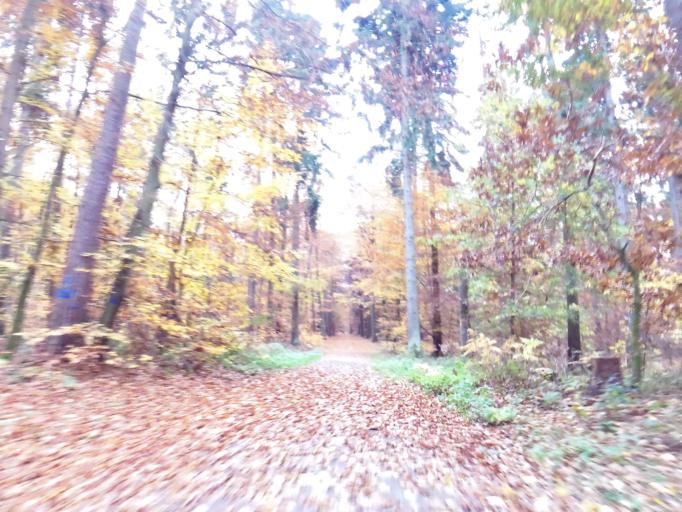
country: DE
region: Hesse
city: Morfelden-Walldorf
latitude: 49.9991
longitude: 8.5927
